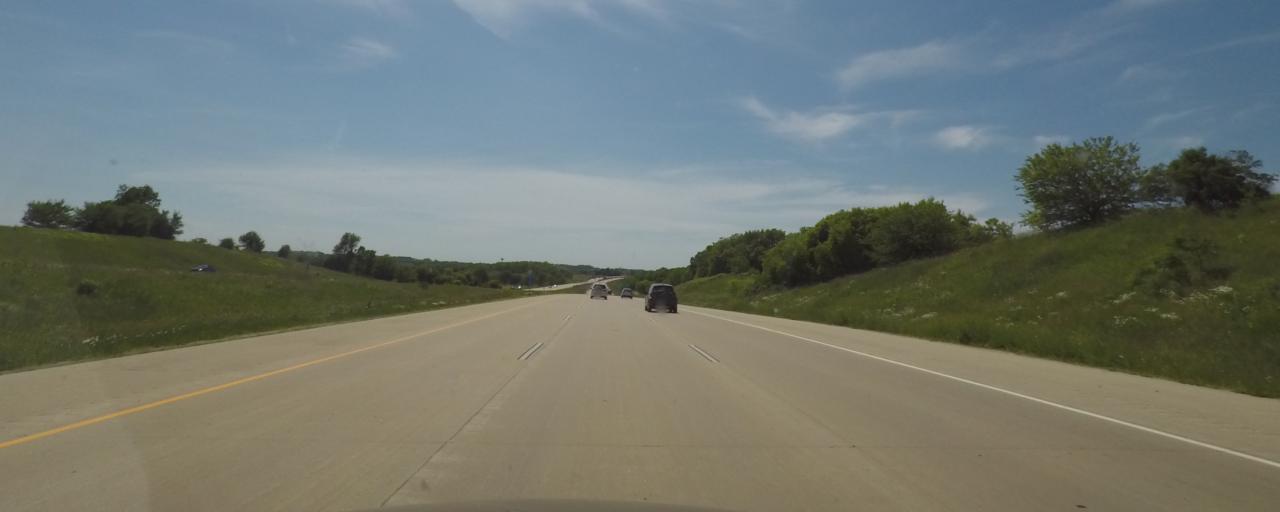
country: US
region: Wisconsin
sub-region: Dane County
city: Cottage Grove
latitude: 43.1077
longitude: -89.2340
